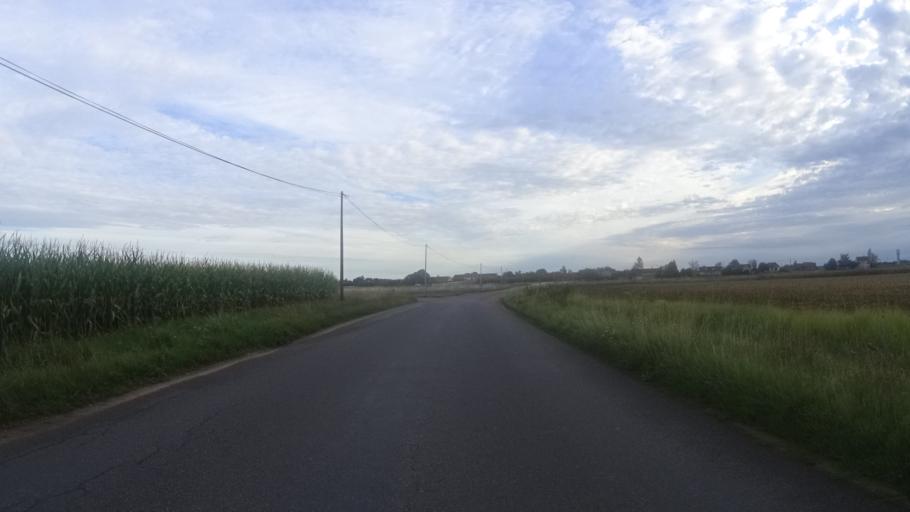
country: FR
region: Centre
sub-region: Departement du Loiret
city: Saint-Benoit-sur-Loire
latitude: 47.7974
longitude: 2.3113
